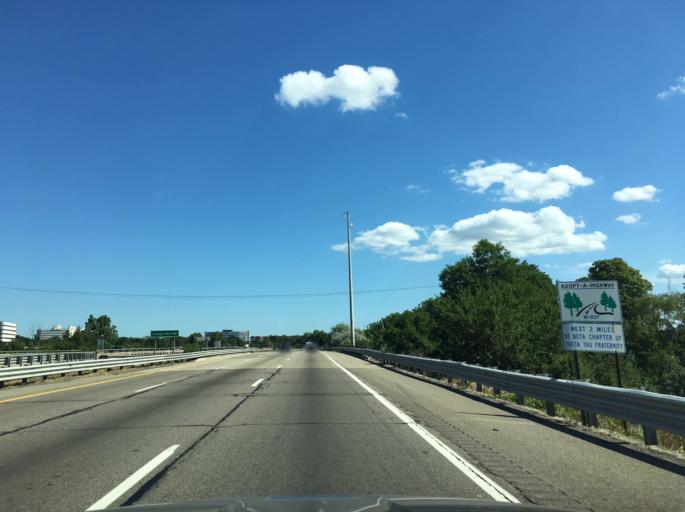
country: US
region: Michigan
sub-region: Oakland County
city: Troy
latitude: 42.5905
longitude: -83.1592
